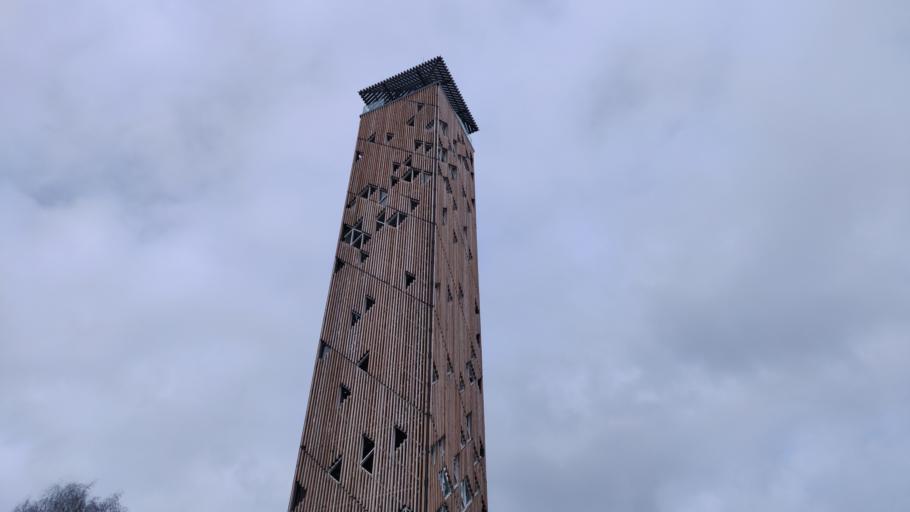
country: LT
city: Birstonas
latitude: 54.6035
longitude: 24.0129
